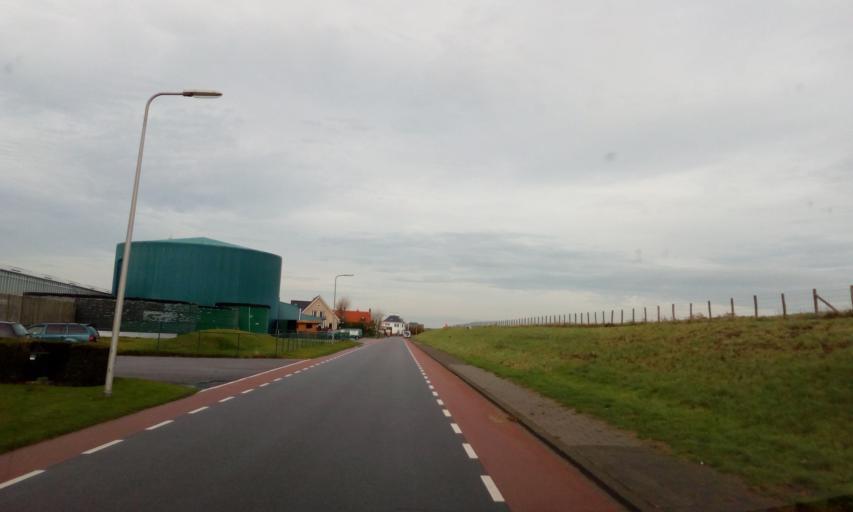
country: NL
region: South Holland
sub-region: Gemeente Westland
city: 's-Gravenzande
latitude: 52.0055
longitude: 4.1509
